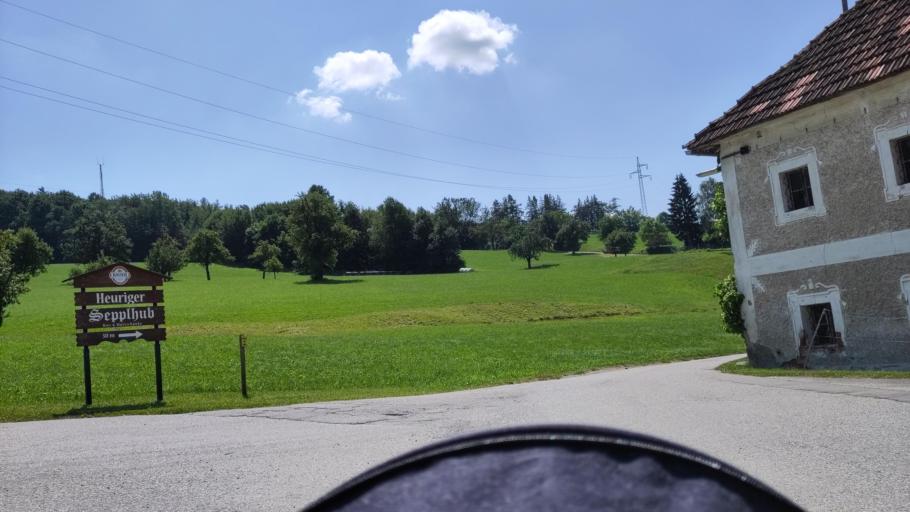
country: AT
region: Upper Austria
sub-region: Politischer Bezirk Steyr-Land
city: Sankt Ulrich bei Steyr
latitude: 48.0331
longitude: 14.4328
